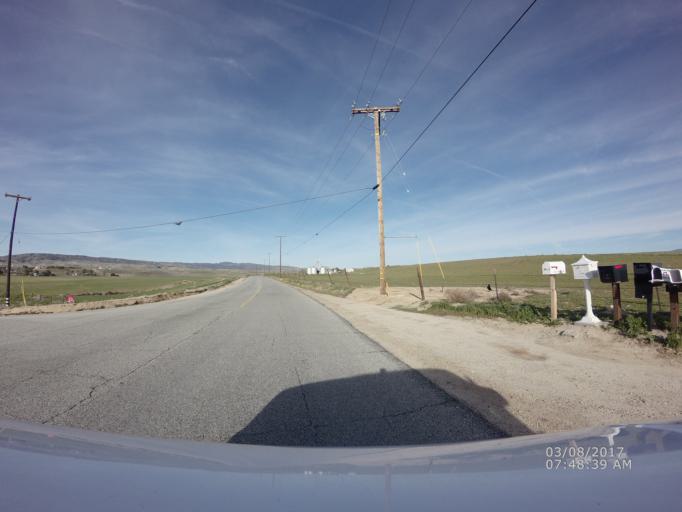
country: US
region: California
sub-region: Los Angeles County
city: Green Valley
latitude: 34.7135
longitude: -118.3515
